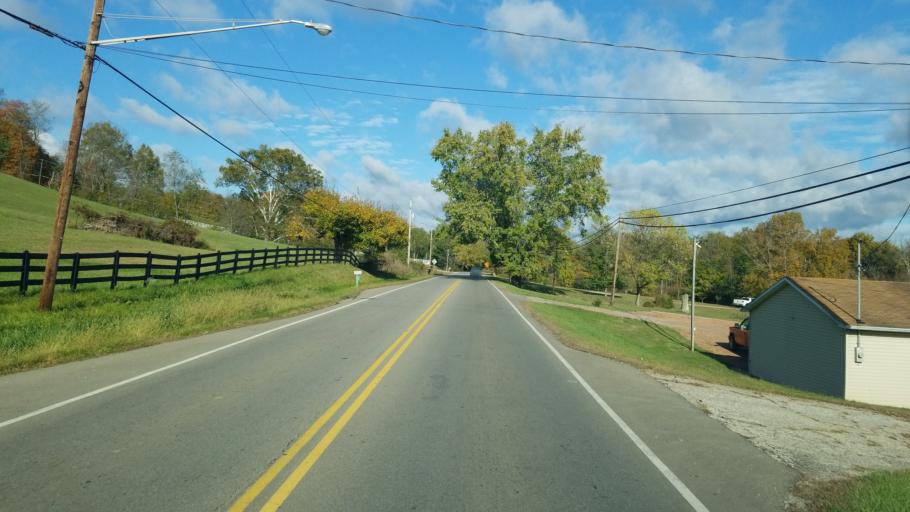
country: US
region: Ohio
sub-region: Jackson County
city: Wellston
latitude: 39.1394
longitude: -82.5297
